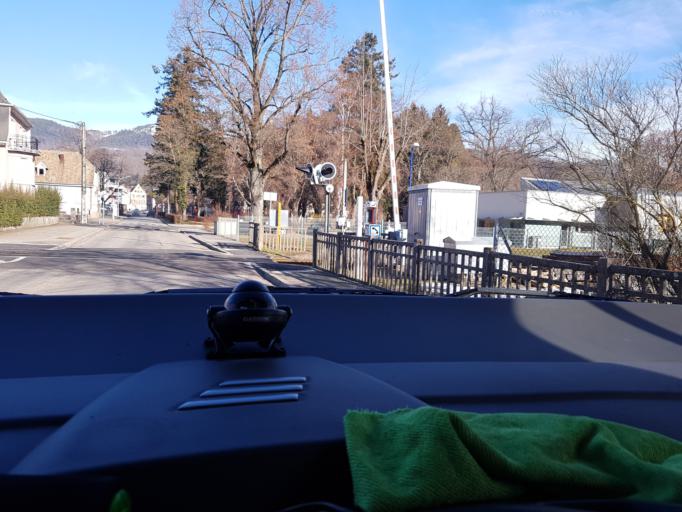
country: FR
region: Alsace
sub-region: Departement du Haut-Rhin
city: Munster
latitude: 48.0380
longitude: 7.1327
